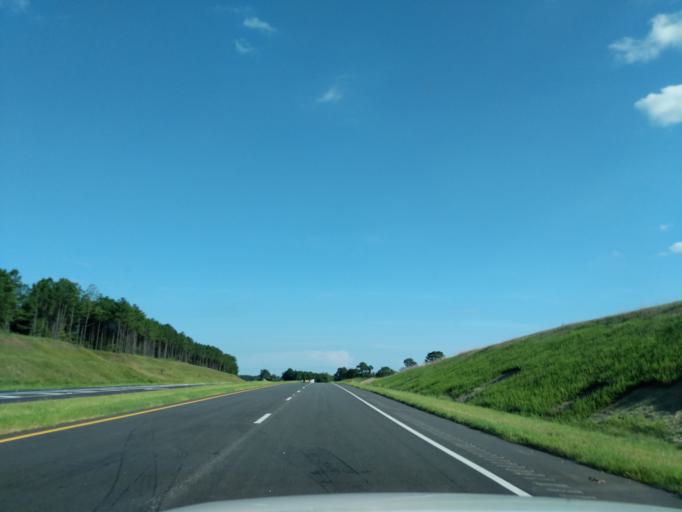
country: US
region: Georgia
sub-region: Wilkes County
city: Washington
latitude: 33.6868
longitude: -82.6426
